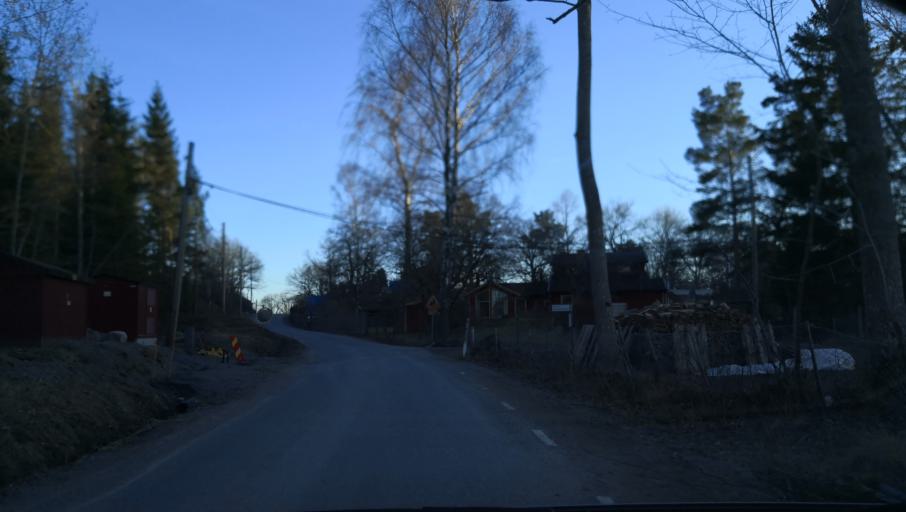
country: SE
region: Stockholm
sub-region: Varmdo Kommun
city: Mortnas
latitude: 59.3377
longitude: 18.4434
